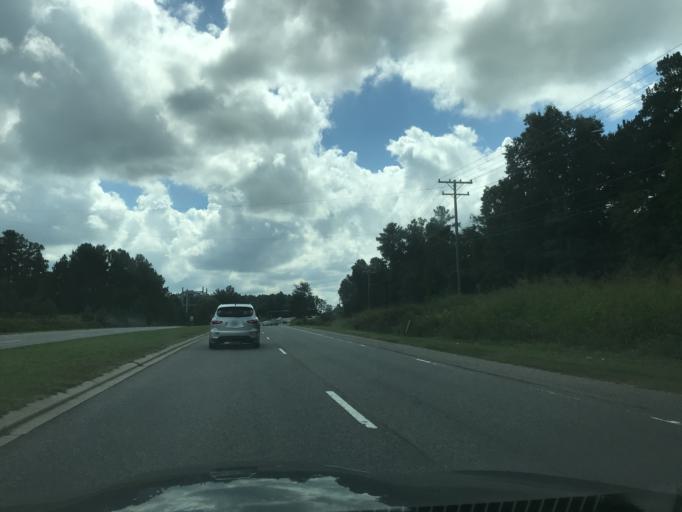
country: US
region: North Carolina
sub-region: Wake County
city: Morrisville
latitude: 35.8776
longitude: -78.8917
